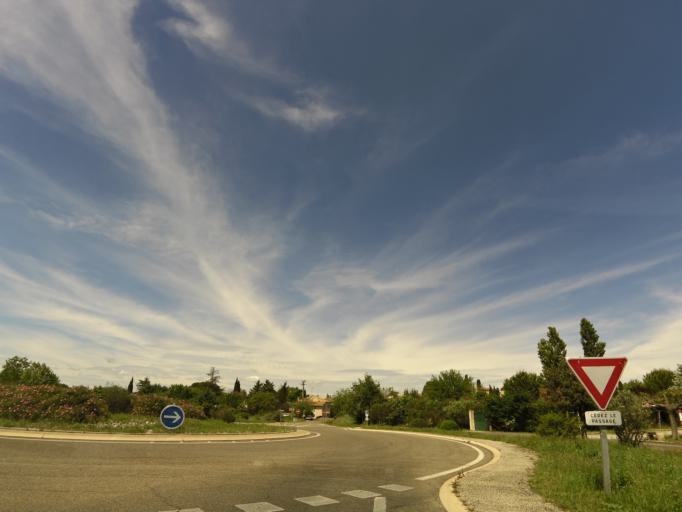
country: FR
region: Languedoc-Roussillon
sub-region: Departement du Gard
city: Villevieille
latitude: 43.7869
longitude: 4.1235
